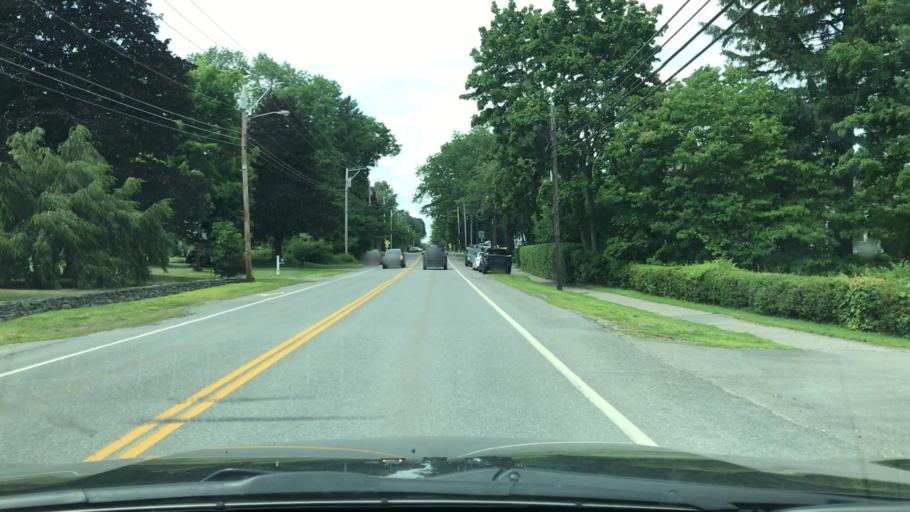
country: US
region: Maine
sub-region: Waldo County
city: Belfast
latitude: 44.4168
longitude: -68.9974
